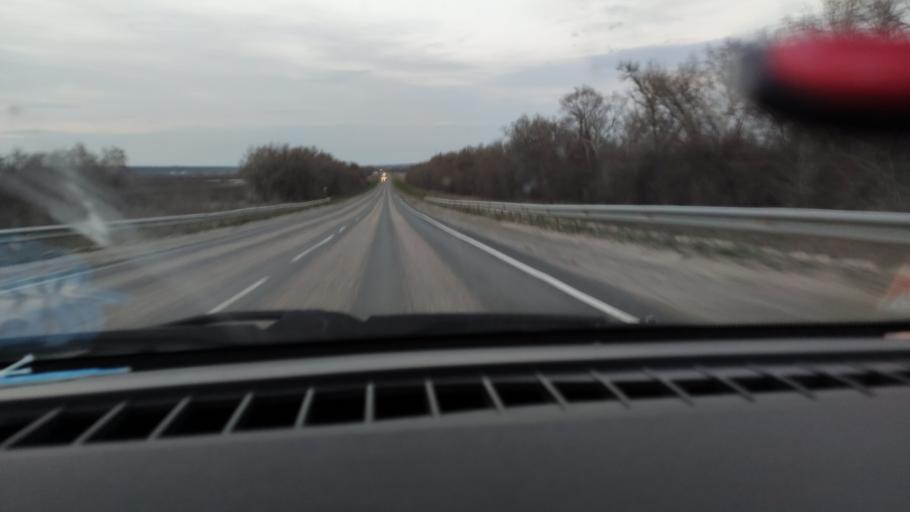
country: RU
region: Saratov
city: Sinodskoye
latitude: 51.9674
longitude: 46.6357
